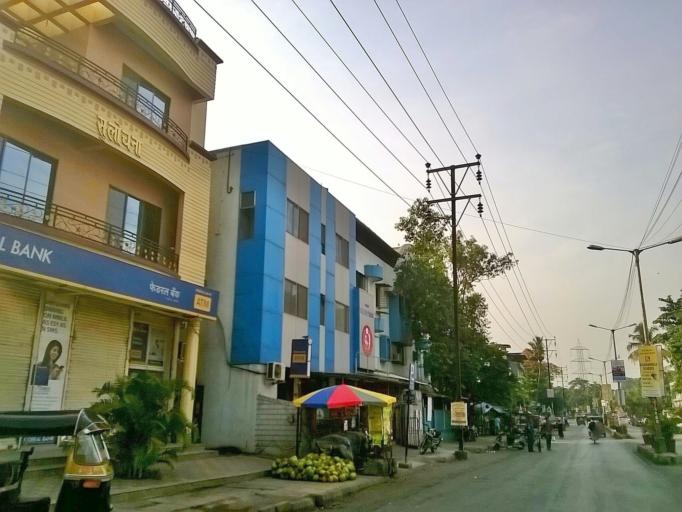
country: IN
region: Maharashtra
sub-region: Raigarh
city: Panvel
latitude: 18.9962
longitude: 73.1192
